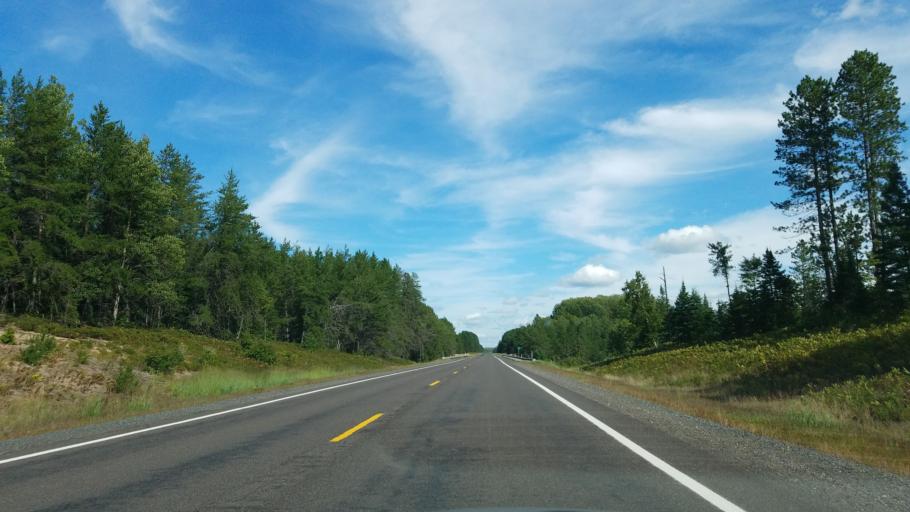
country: US
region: Michigan
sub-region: Baraga County
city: Baraga
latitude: 46.5062
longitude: -88.7447
